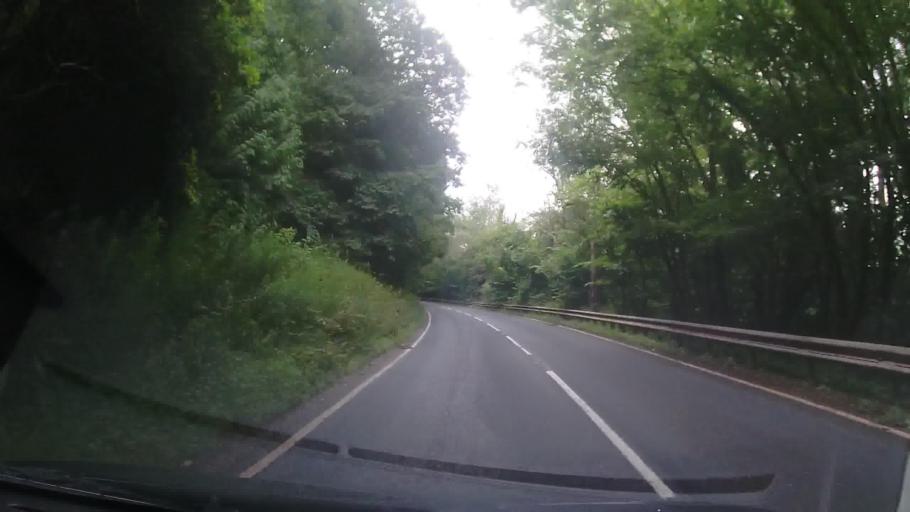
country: GB
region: Wales
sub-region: Sir Powys
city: Knighton
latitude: 52.3460
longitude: -3.0218
